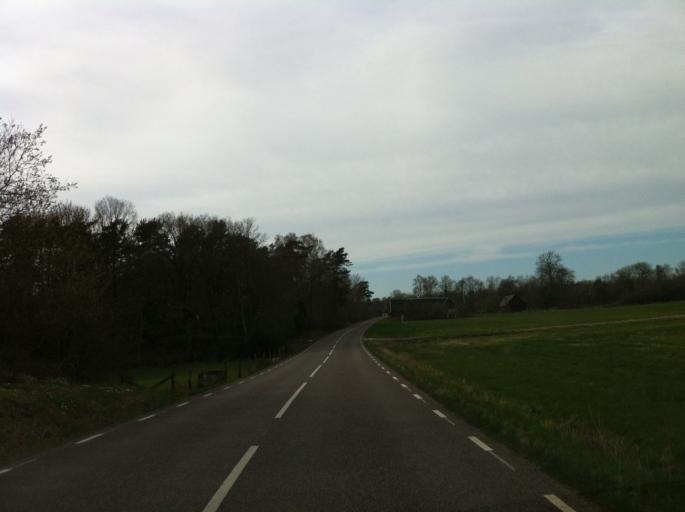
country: SE
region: Skane
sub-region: Hoganas Kommun
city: Hoganas
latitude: 56.2560
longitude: 12.6150
